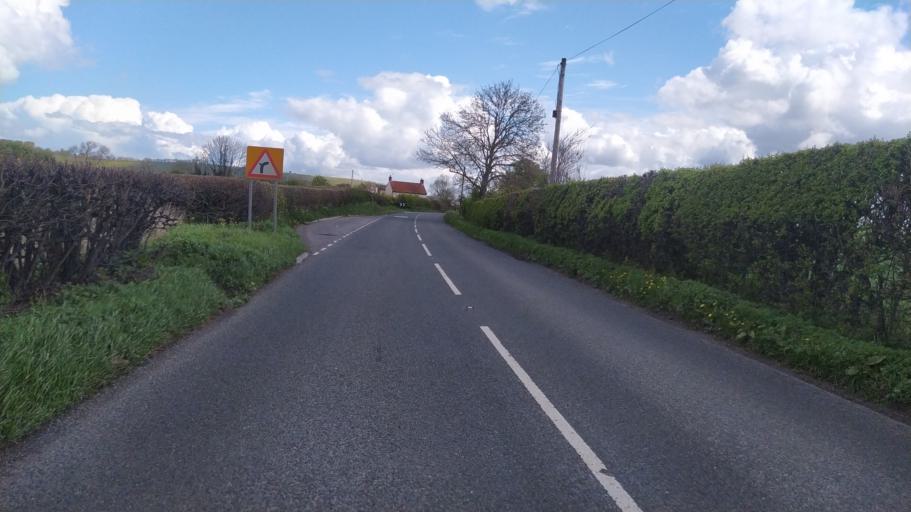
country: GB
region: England
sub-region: Wiltshire
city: Kilmington
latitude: 51.1187
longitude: -2.3045
